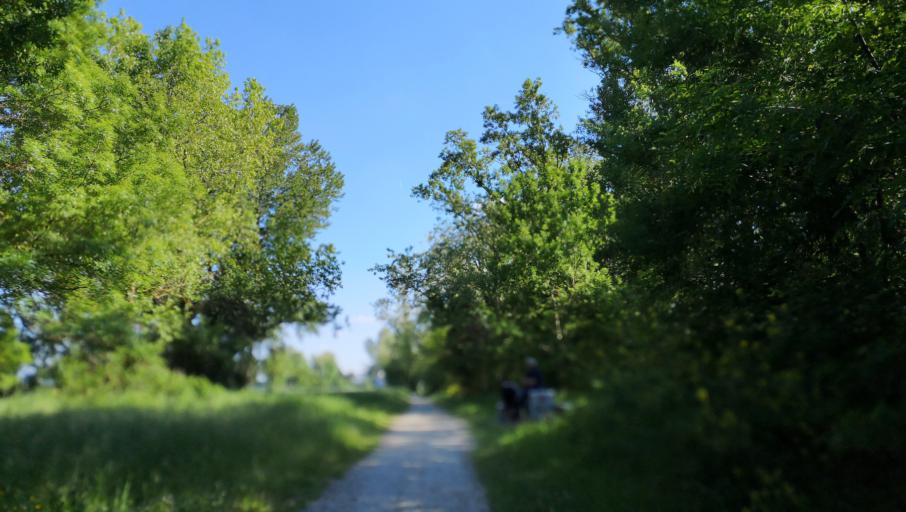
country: FR
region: Midi-Pyrenees
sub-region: Departement de la Haute-Garonne
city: Blagnac
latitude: 43.6436
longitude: 1.4034
